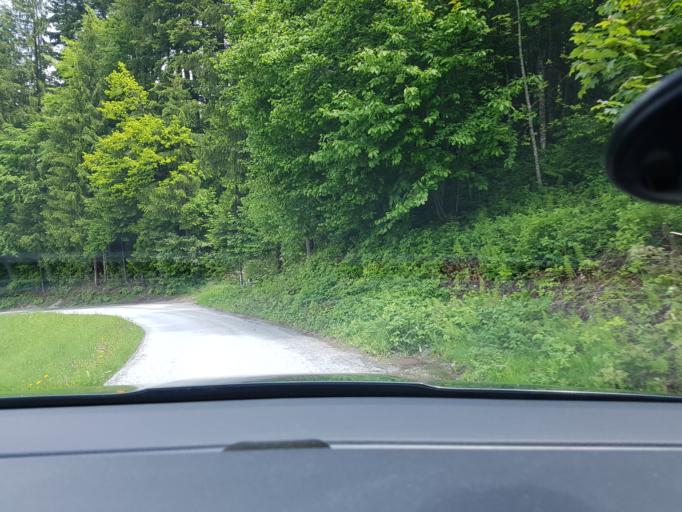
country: AT
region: Tyrol
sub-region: Politischer Bezirk Kufstein
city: Soll
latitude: 47.4955
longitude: 12.2024
